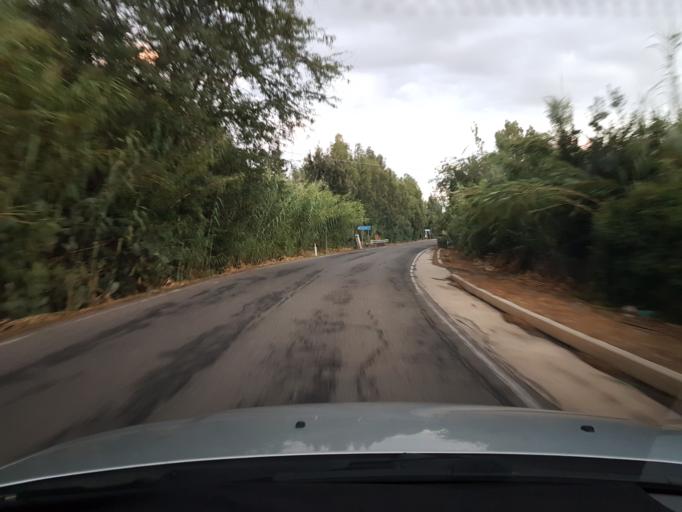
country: IT
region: Sardinia
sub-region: Provincia di Oristano
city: Milis
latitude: 40.0415
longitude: 8.6360
